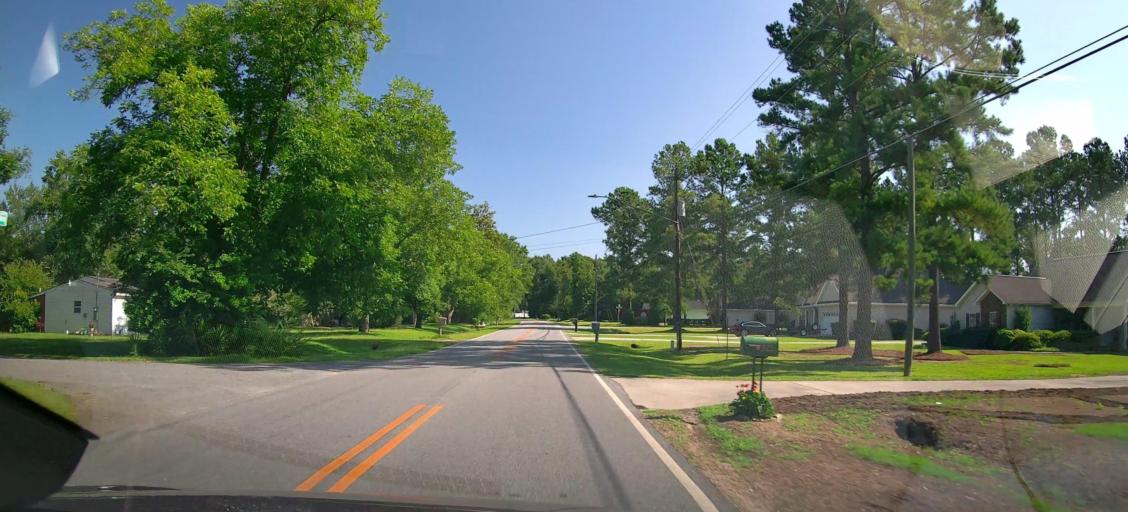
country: US
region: Georgia
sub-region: Peach County
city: Byron
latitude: 32.7334
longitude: -83.7039
